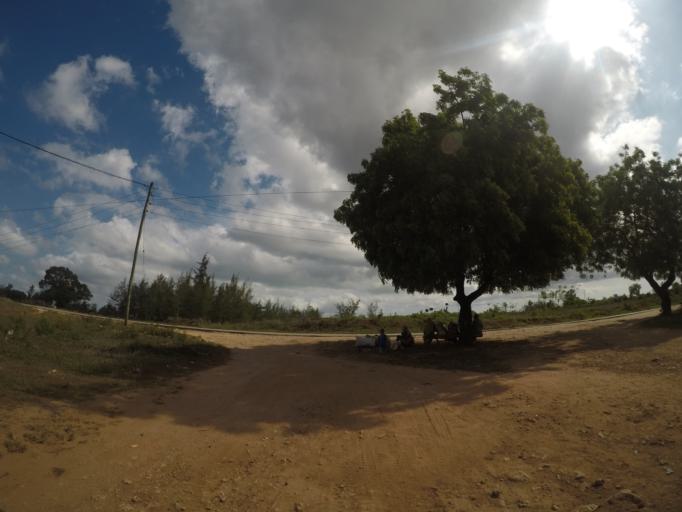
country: TZ
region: Zanzibar Central/South
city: Koani
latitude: -6.2007
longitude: 39.3142
